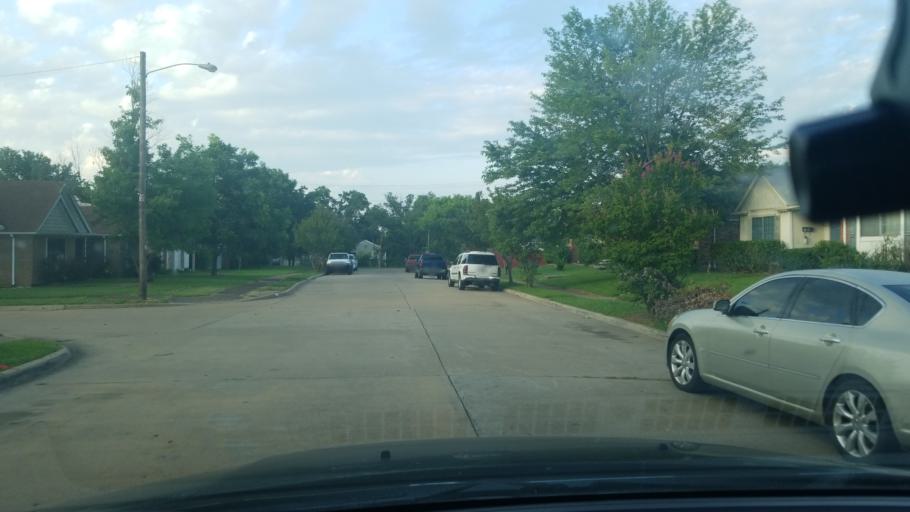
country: US
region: Texas
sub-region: Dallas County
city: Balch Springs
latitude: 32.7287
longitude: -96.6502
